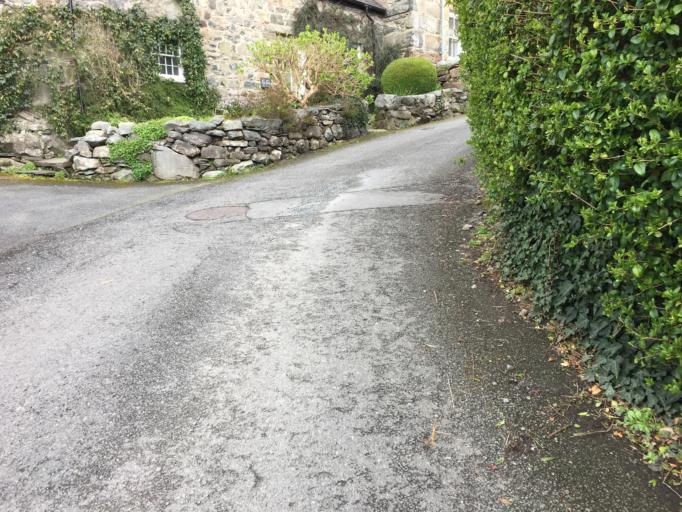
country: GB
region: Wales
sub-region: Gwynedd
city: Llanfair
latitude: 52.8598
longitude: -4.1077
